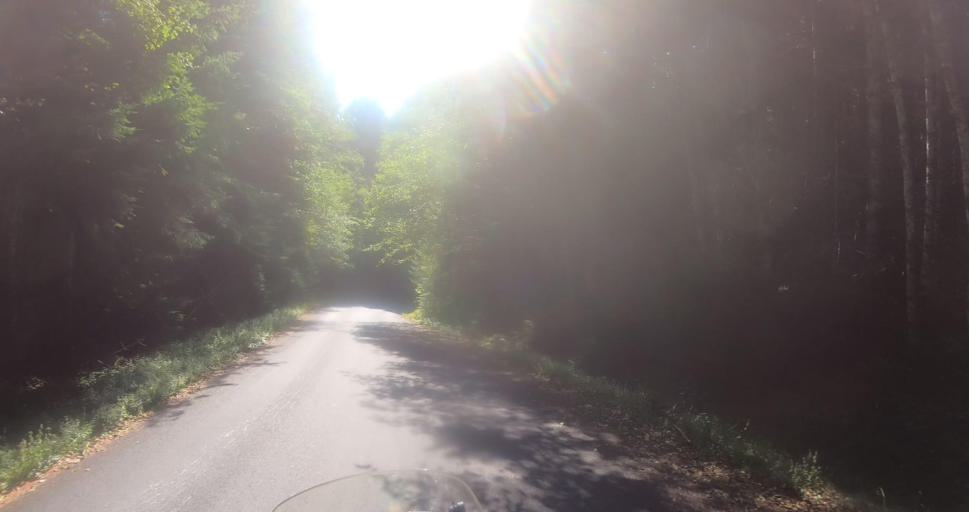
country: US
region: Washington
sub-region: Skamania County
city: Carson
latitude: 46.1704
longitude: -121.8636
